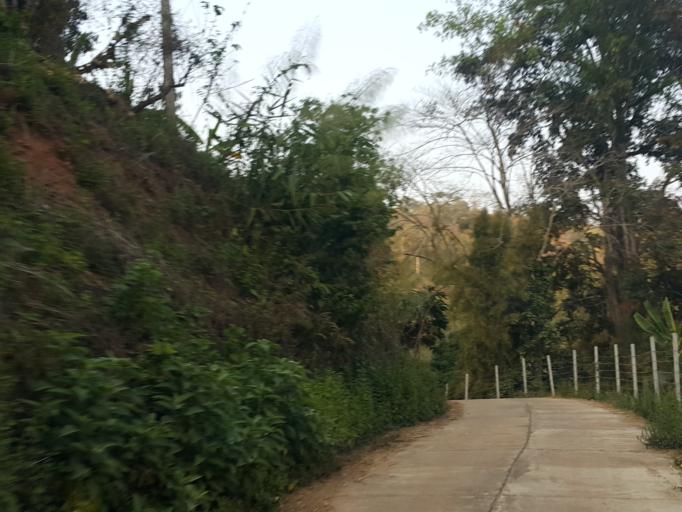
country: TH
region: Chiang Mai
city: Mae Taeng
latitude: 19.0683
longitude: 98.7738
